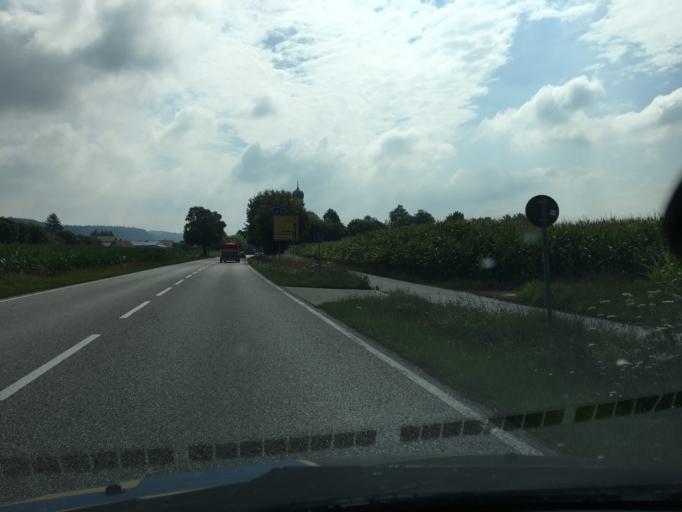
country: DE
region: Bavaria
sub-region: Upper Bavaria
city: Winhoring
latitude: 48.2634
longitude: 12.6459
